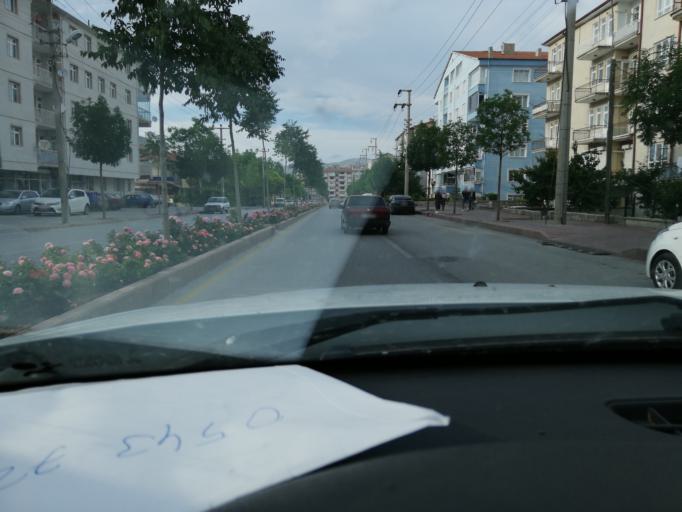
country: TR
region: Kirsehir
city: Kirsehir
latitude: 39.1376
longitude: 34.1598
